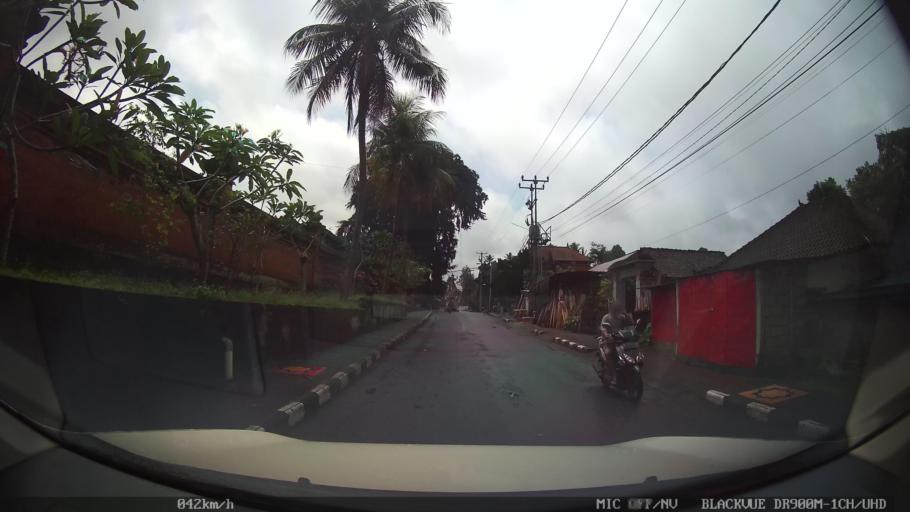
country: ID
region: Bali
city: Pegongan
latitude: -8.4888
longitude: 115.2263
